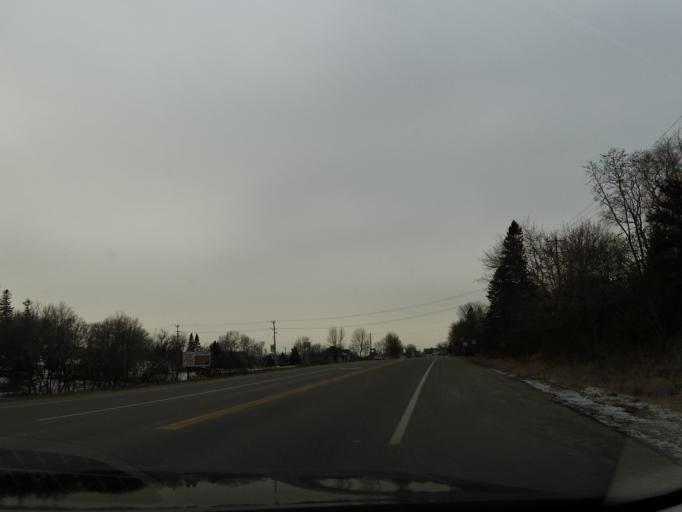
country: US
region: Minnesota
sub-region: Carver County
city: Waconia
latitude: 44.8451
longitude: -93.7786
